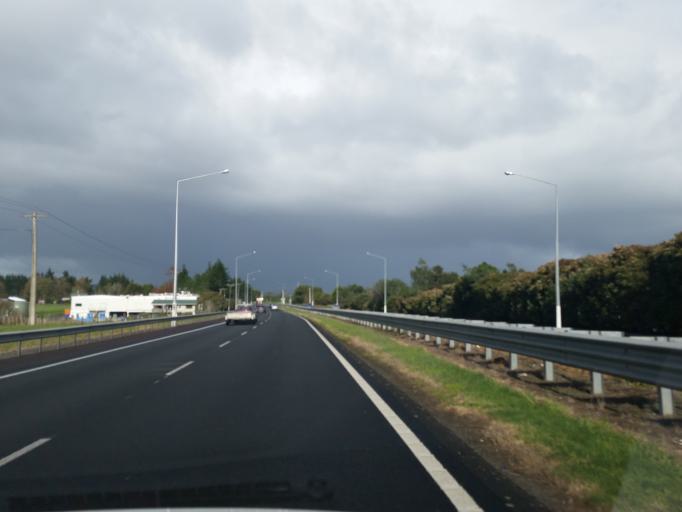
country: NZ
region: Auckland
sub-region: Auckland
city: Papakura
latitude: -37.1119
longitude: 174.9475
